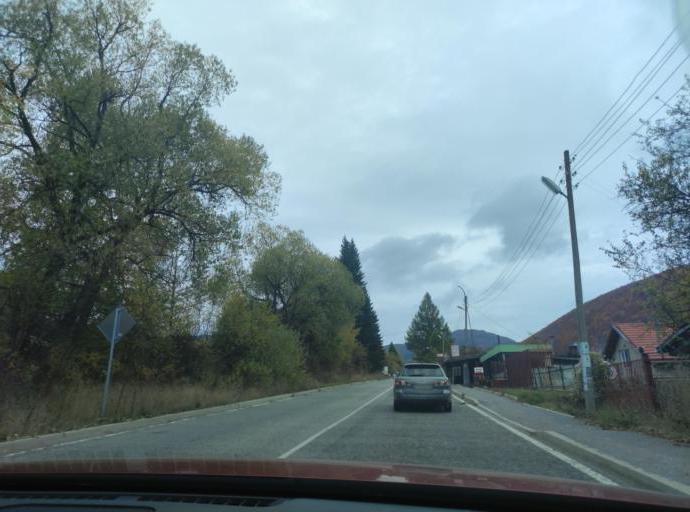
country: BG
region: Sofiya
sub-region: Obshtina Godech
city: Godech
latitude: 43.0926
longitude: 23.0984
